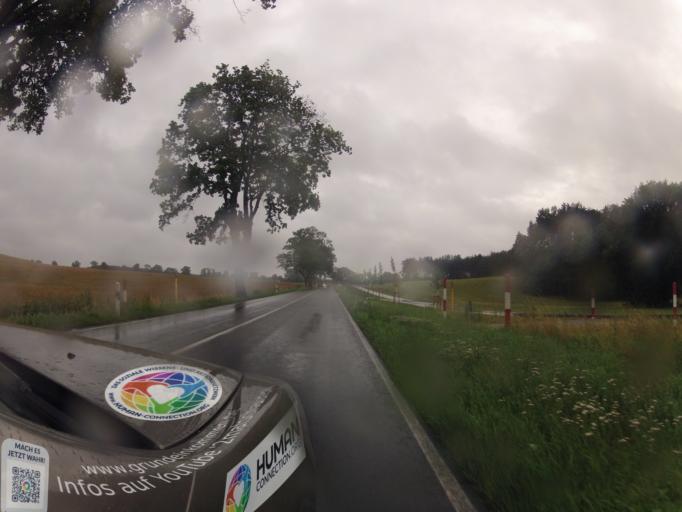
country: DE
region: Mecklenburg-Vorpommern
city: Seebad Heringsdorf
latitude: 53.8978
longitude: 14.1447
